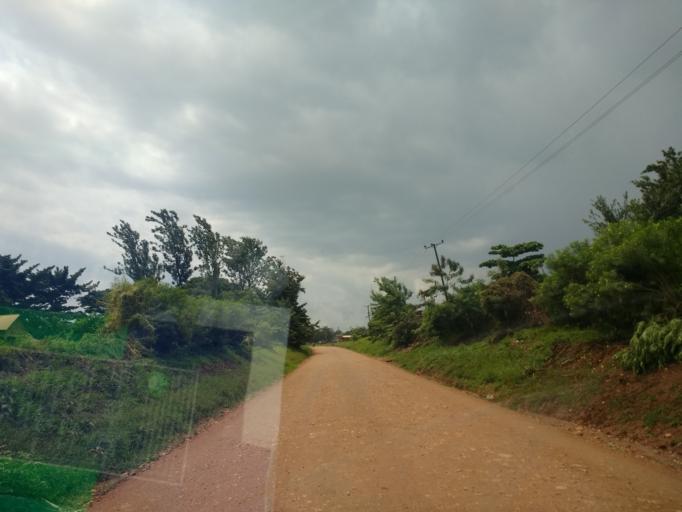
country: UG
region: Eastern Region
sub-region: Sironko District
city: Sironko
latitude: 1.3373
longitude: 34.2983
